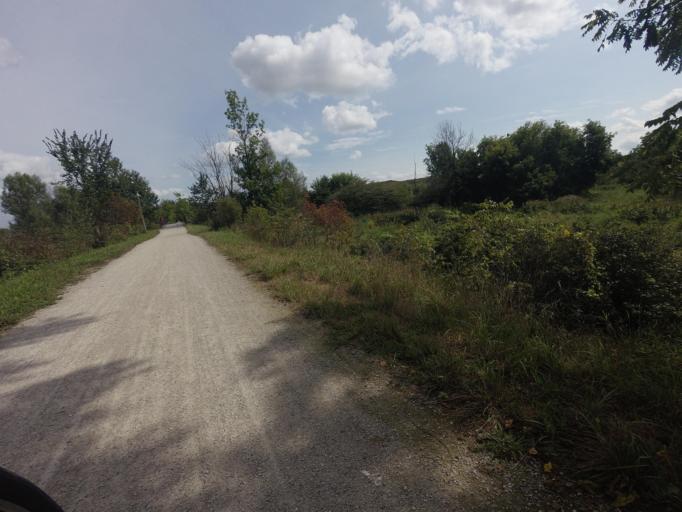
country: CA
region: Ontario
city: Waterloo
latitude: 43.6115
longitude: -80.5704
